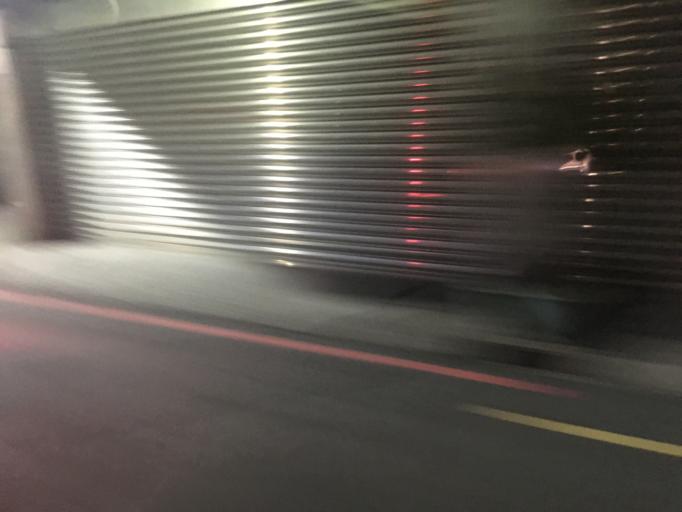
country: TW
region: Taiwan
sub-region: Hsinchu
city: Hsinchu
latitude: 24.8354
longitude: 120.9452
